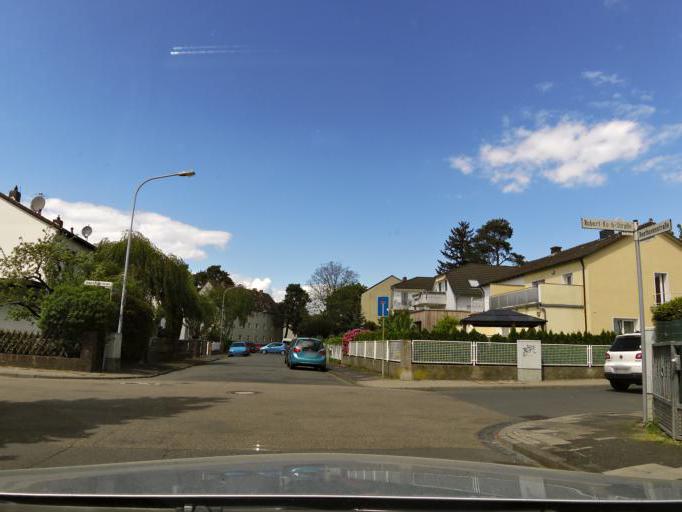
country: DE
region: Hesse
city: Langen
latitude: 49.9913
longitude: 8.6512
